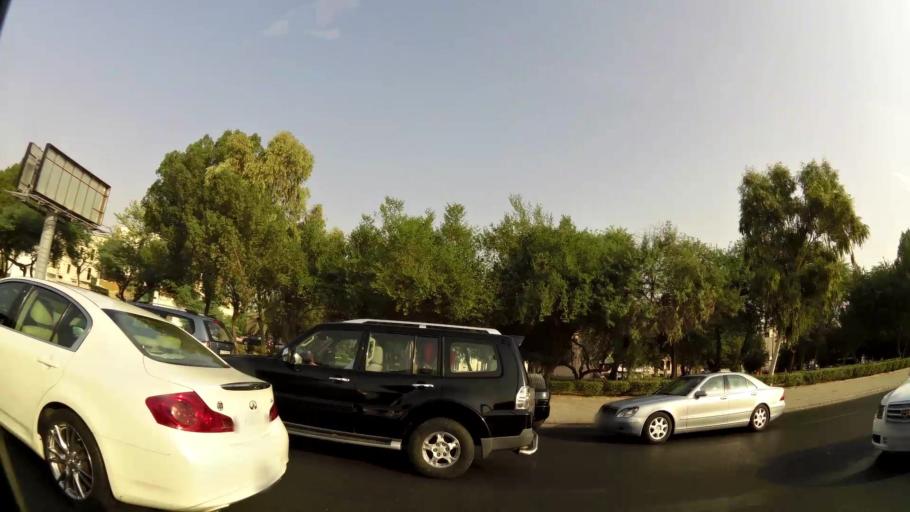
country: KW
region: Al Asimah
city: Ash Shamiyah
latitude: 29.3203
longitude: 47.9894
